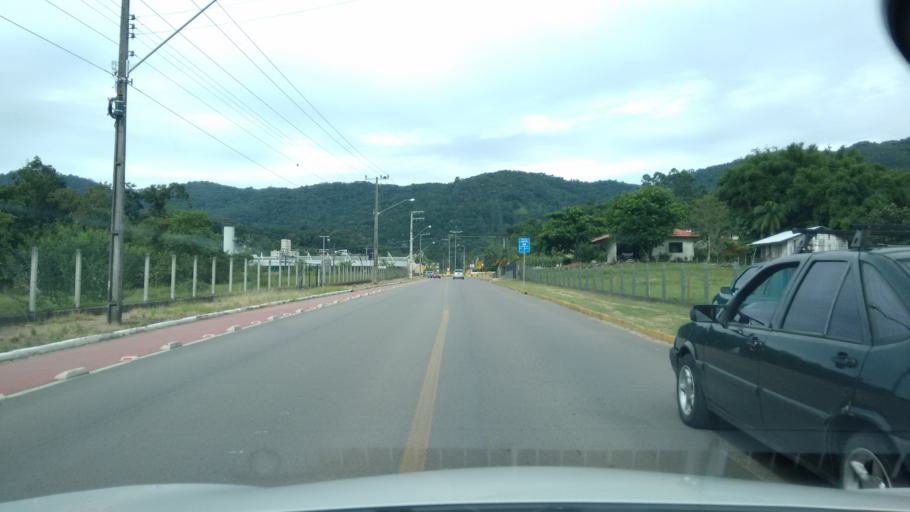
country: BR
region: Santa Catarina
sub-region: Timbo
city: Timbo
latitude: -26.8088
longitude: -49.2531
